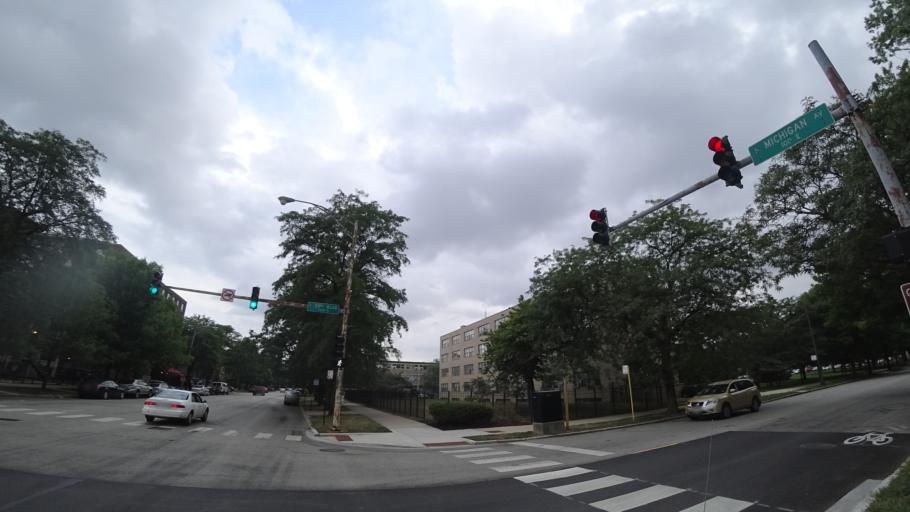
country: US
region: Illinois
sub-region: Cook County
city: Chicago
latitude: 41.8348
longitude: -87.6234
